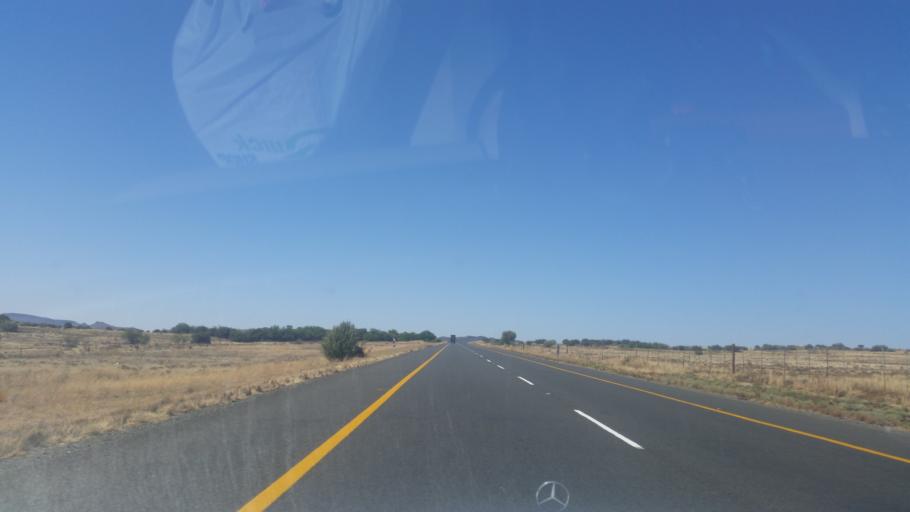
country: ZA
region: Northern Cape
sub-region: Pixley ka Seme District Municipality
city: Colesberg
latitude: -30.5745
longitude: 25.4454
